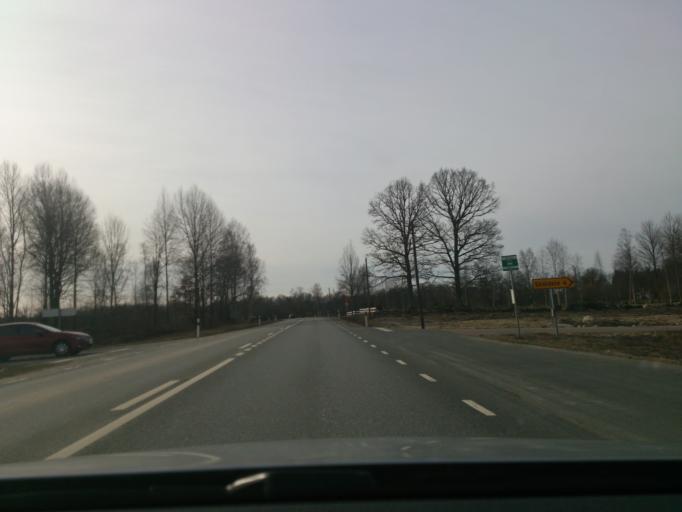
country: SE
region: Kronoberg
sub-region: Alvesta Kommun
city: Alvesta
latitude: 56.9354
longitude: 14.5590
